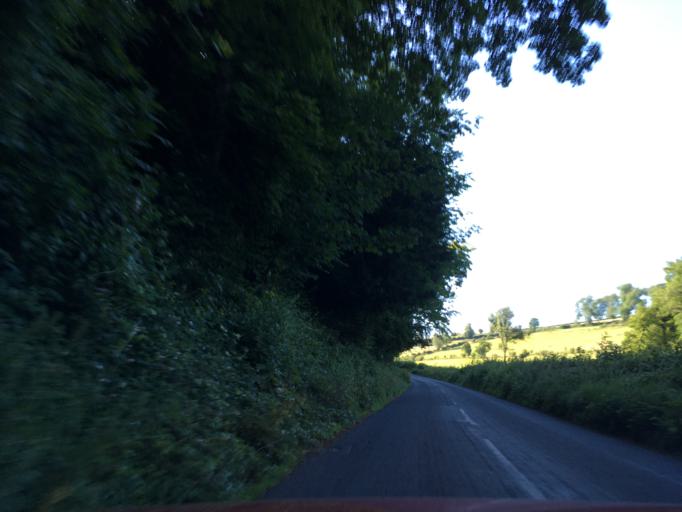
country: GB
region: England
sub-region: Gloucestershire
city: Coleford
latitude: 51.7931
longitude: -2.6595
